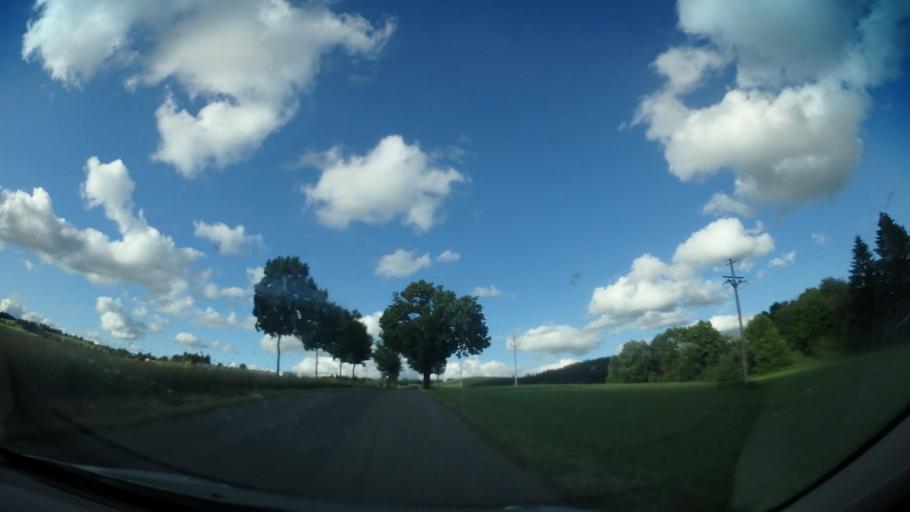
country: CZ
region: Vysocina
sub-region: Okres Zd'ar nad Sazavou
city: Jimramov
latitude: 49.5699
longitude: 16.1843
